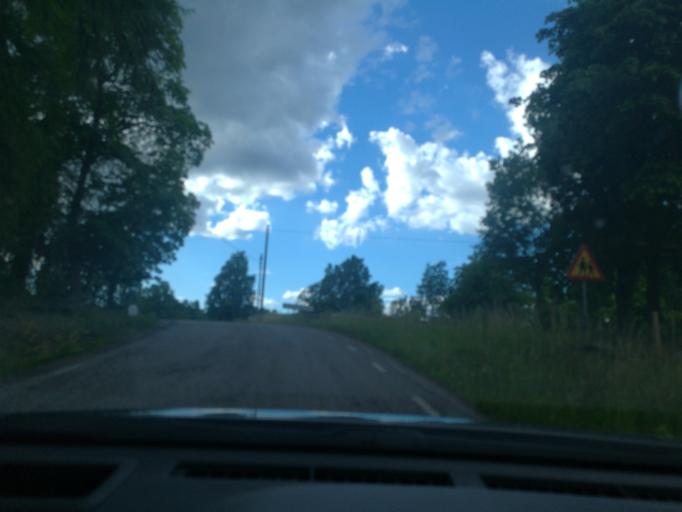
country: SE
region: Soedermanland
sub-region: Eskilstuna Kommun
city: Arla
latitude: 59.4426
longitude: 16.7863
